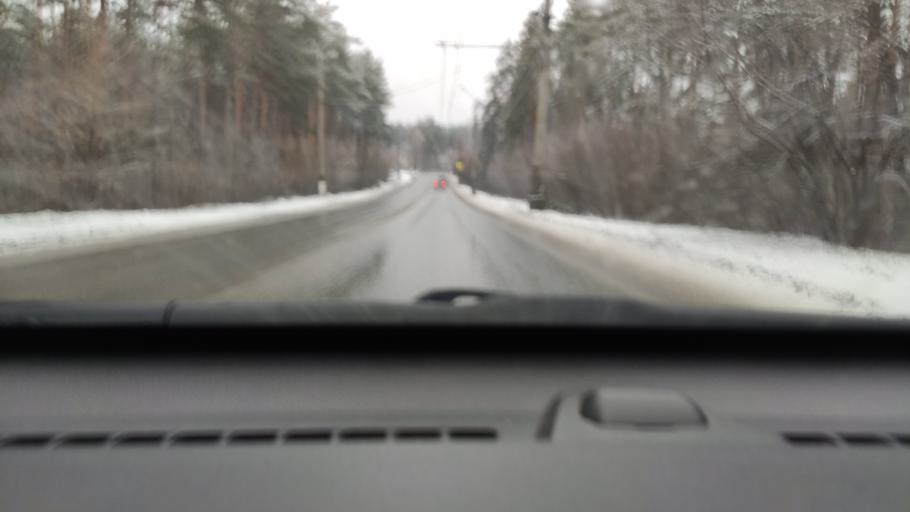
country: RU
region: Samara
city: Tol'yatti
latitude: 53.4793
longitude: 49.3619
